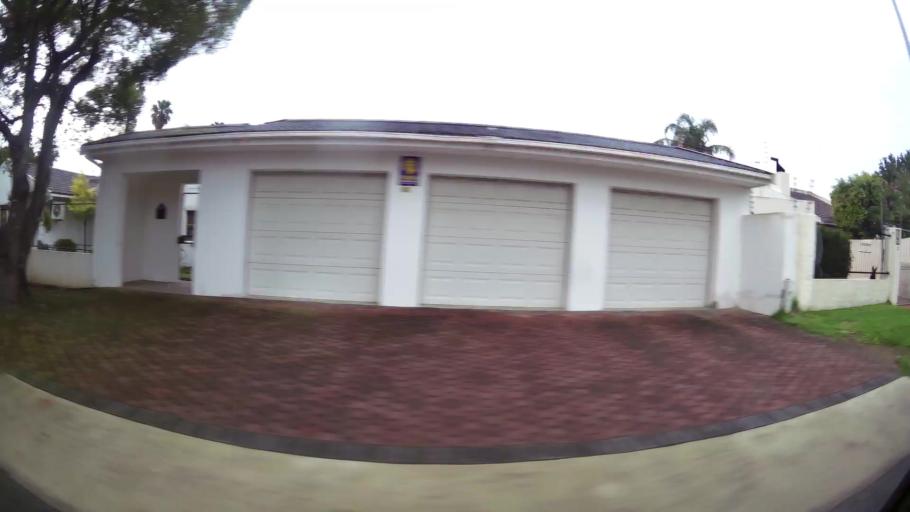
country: ZA
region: Eastern Cape
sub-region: Nelson Mandela Bay Metropolitan Municipality
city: Port Elizabeth
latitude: -33.9947
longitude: 25.5541
